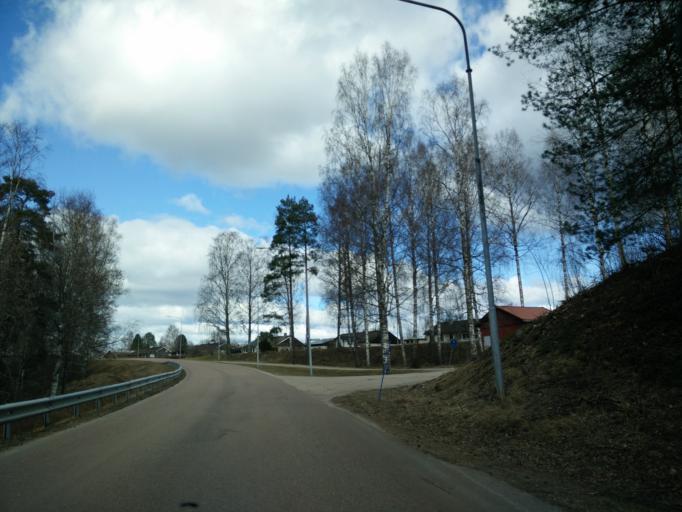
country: SE
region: Vaermland
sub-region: Hagfors Kommun
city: Hagfors
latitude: 60.0019
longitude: 13.5980
